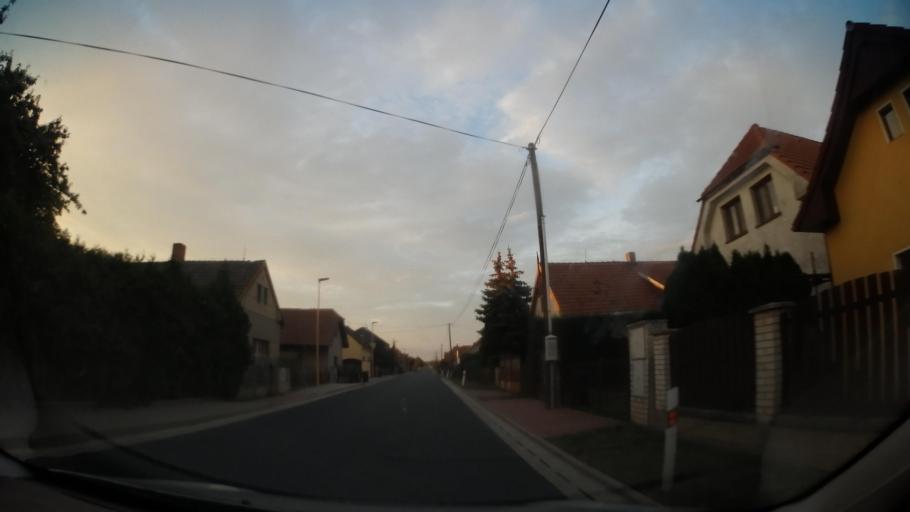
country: CZ
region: Central Bohemia
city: Loucen
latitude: 50.2423
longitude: 15.0228
